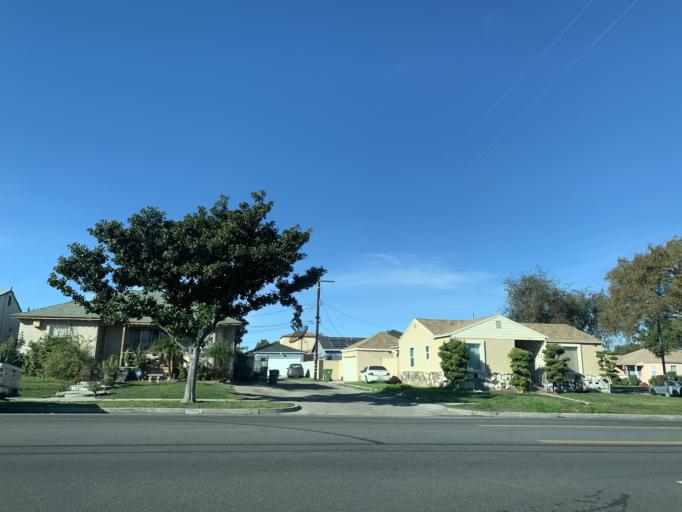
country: US
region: California
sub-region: Los Angeles County
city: West Athens
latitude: 33.9262
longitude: -118.2868
